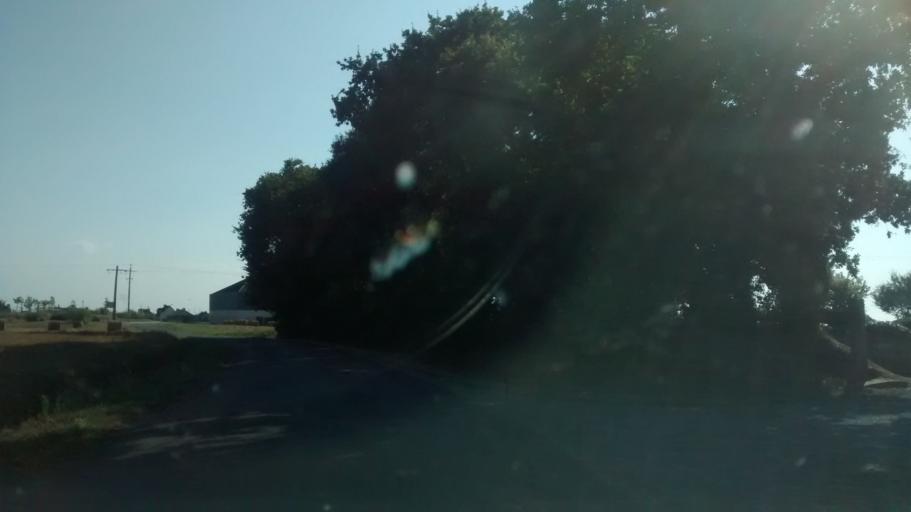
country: FR
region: Brittany
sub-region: Departement d'Ille-et-Vilaine
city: Saint-Coulomb
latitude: 48.6836
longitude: -1.9114
